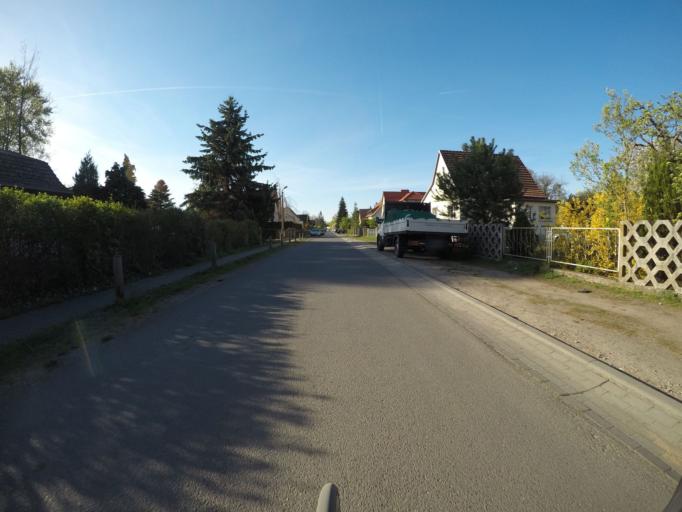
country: DE
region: Brandenburg
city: Neuenhagen
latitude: 52.5167
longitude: 13.7129
